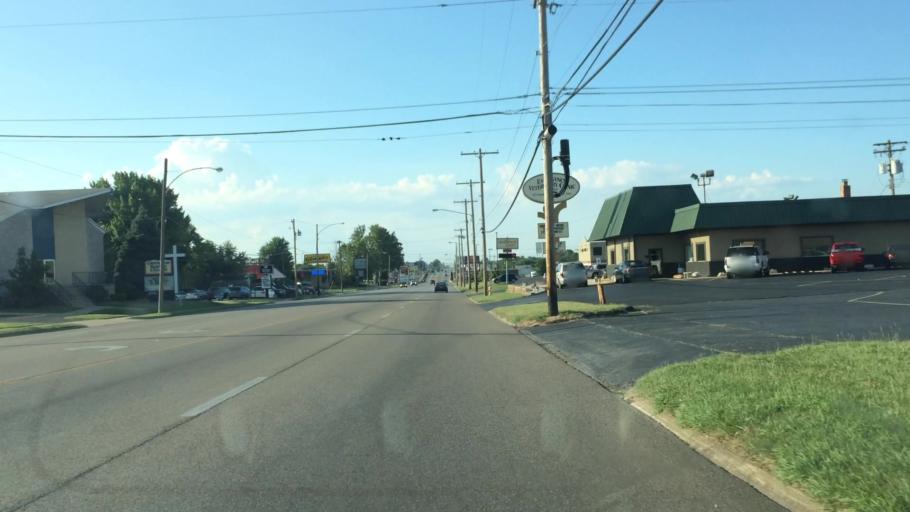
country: US
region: Missouri
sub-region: Greene County
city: Springfield
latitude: 37.2054
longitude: -93.2619
